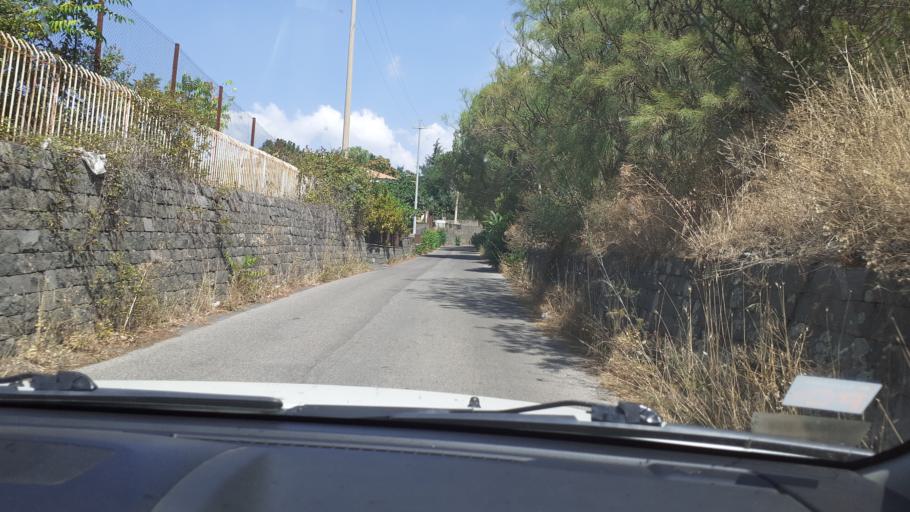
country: IT
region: Sicily
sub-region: Catania
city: Nicolosi
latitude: 37.6280
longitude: 15.0245
